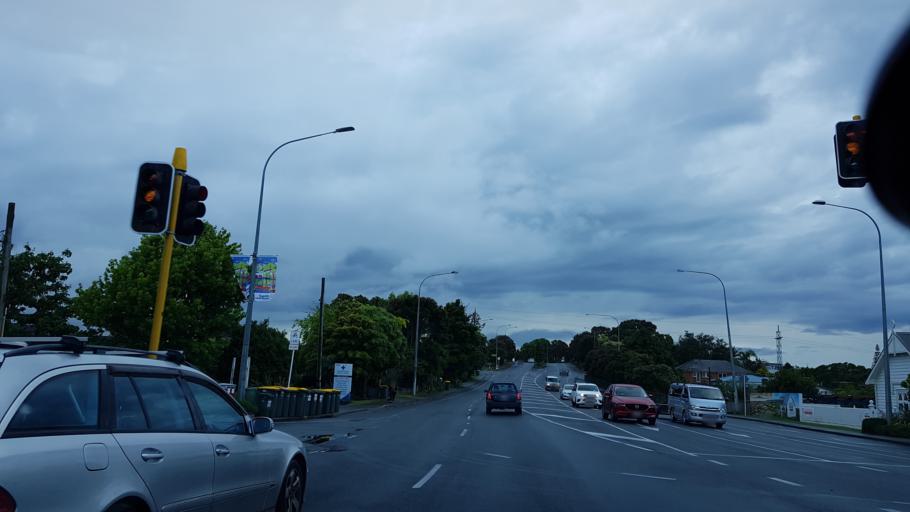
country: NZ
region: Auckland
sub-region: Auckland
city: North Shore
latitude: -36.7807
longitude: 174.7216
